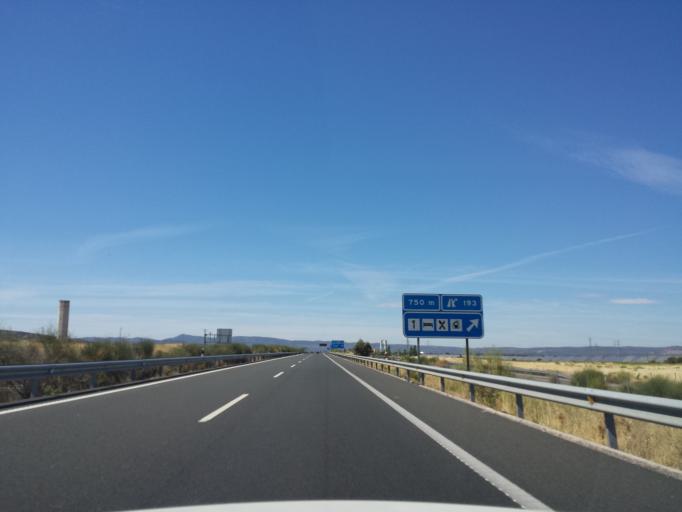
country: ES
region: Extremadura
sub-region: Provincia de Caceres
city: Saucedilla
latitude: 39.8362
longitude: -5.6500
